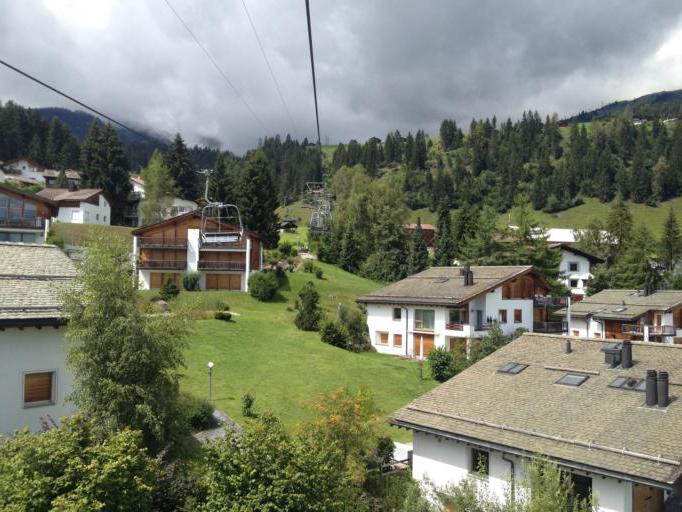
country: CH
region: Grisons
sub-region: Imboden District
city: Flims
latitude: 46.8375
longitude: 9.2776
